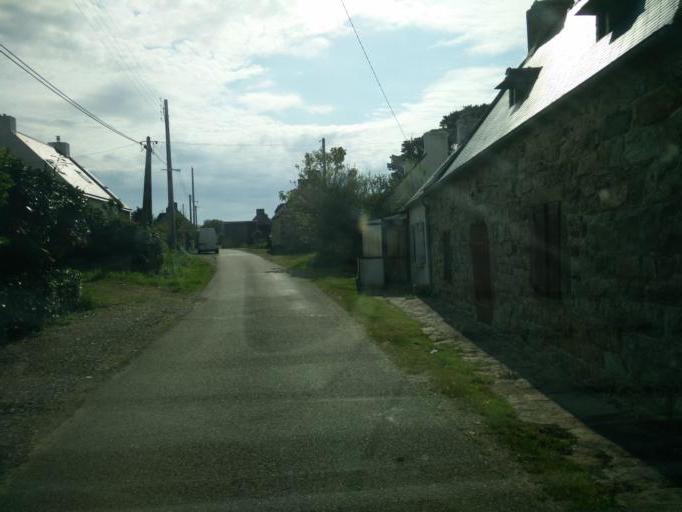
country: FR
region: Brittany
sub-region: Departement du Finistere
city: Crozon
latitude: 48.2347
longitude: -4.5488
